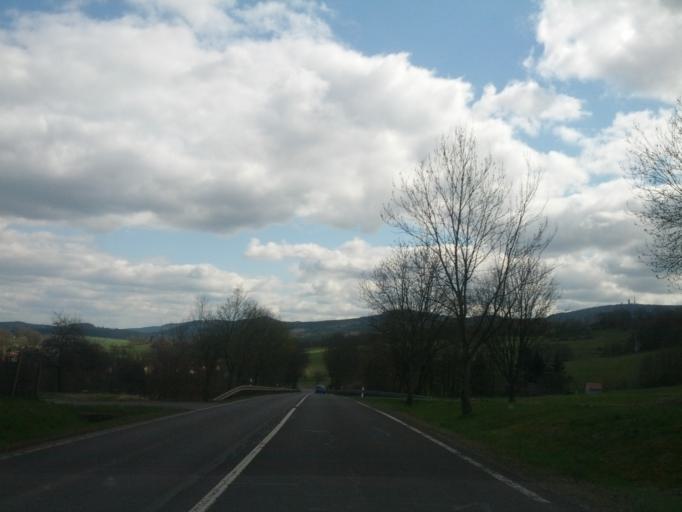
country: DE
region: Thuringia
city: Seebach
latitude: 50.9025
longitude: 10.4379
